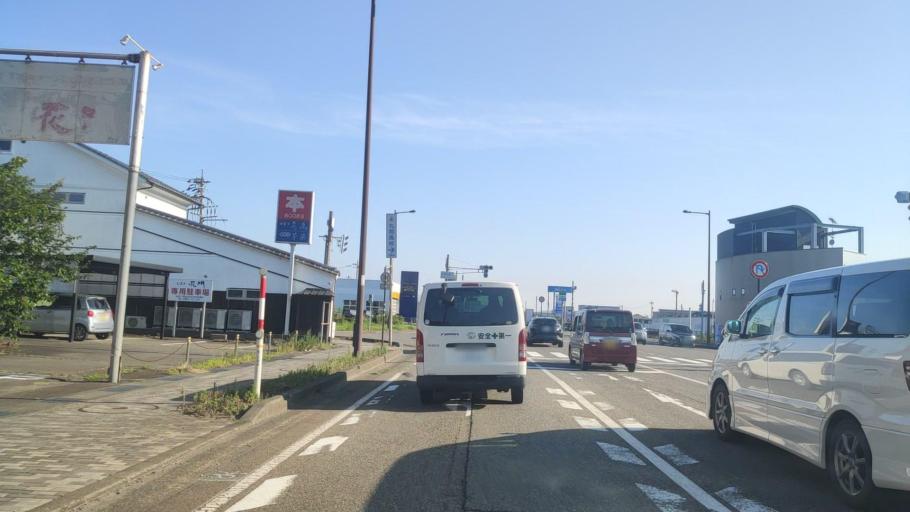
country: JP
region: Fukui
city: Maruoka
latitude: 36.1497
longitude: 136.2648
